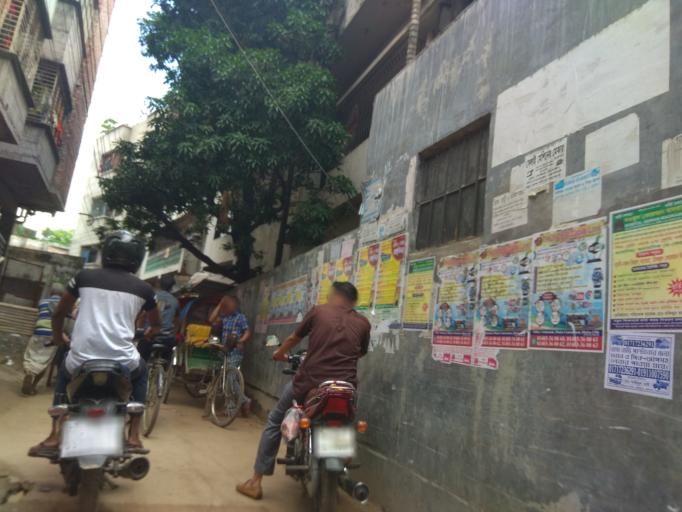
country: BD
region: Dhaka
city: Tungi
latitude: 23.8144
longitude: 90.3899
